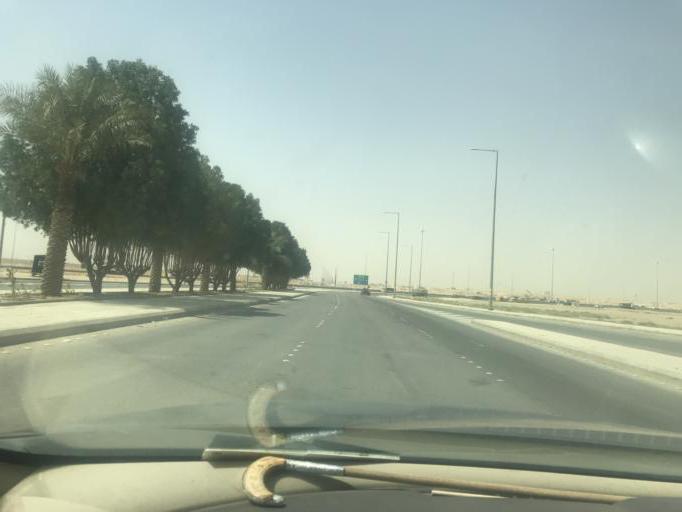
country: SA
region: Ar Riyad
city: Riyadh
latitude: 24.8072
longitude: 46.5804
